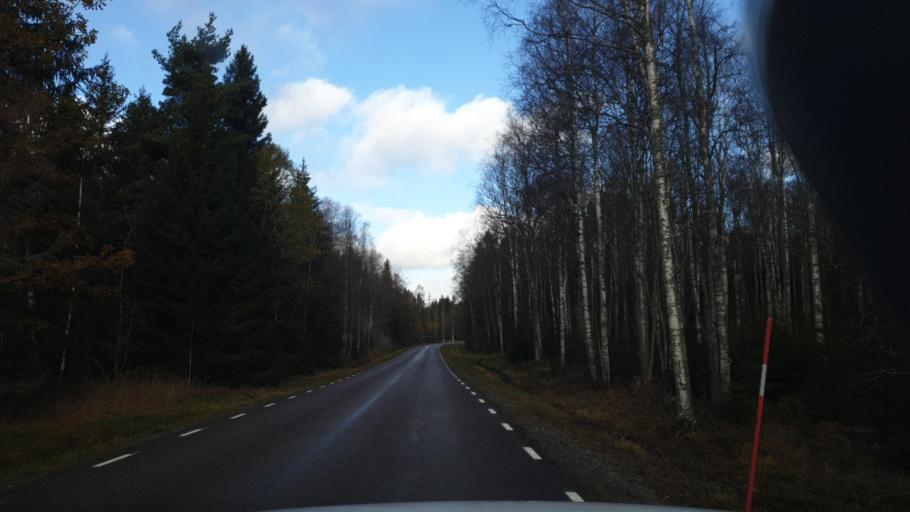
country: SE
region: Vaermland
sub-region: Grums Kommun
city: Slottsbron
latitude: 59.4835
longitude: 12.8829
